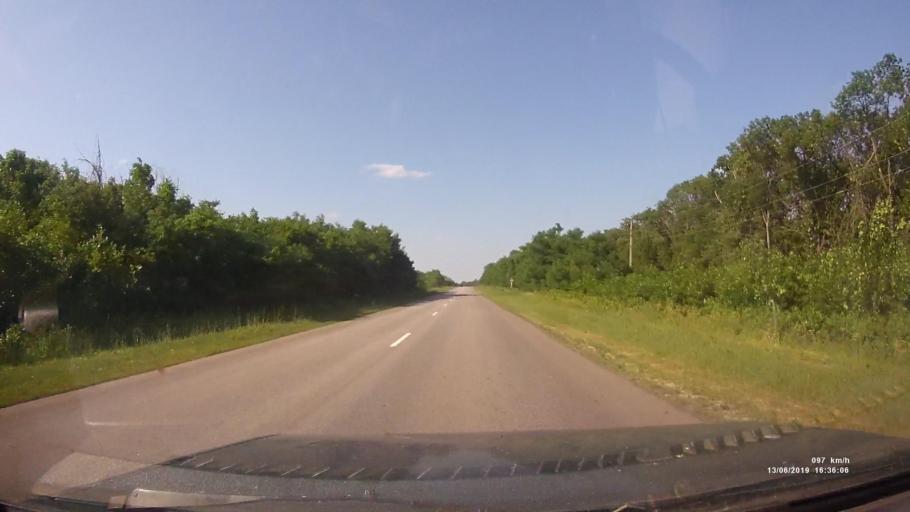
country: RU
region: Rostov
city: Kazanskaya
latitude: 49.8908
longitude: 41.3034
